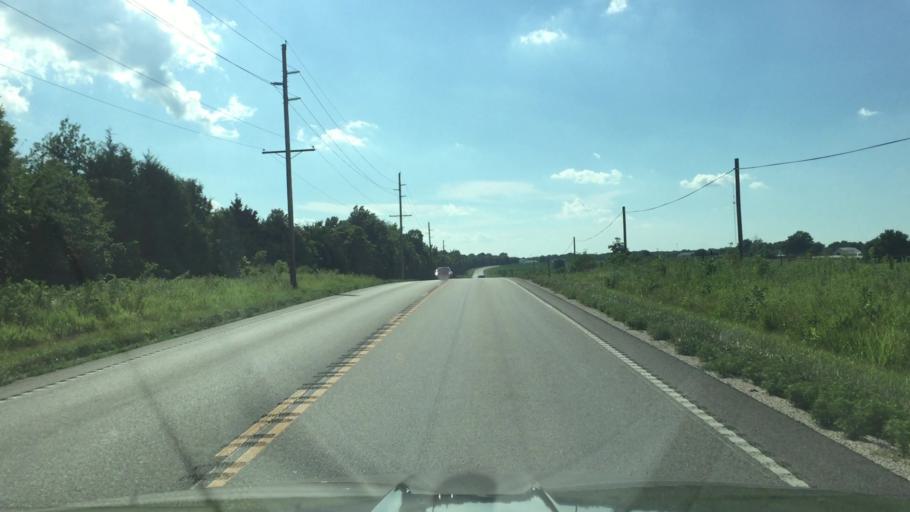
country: US
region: Missouri
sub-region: Morgan County
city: Versailles
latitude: 38.4026
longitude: -92.7490
